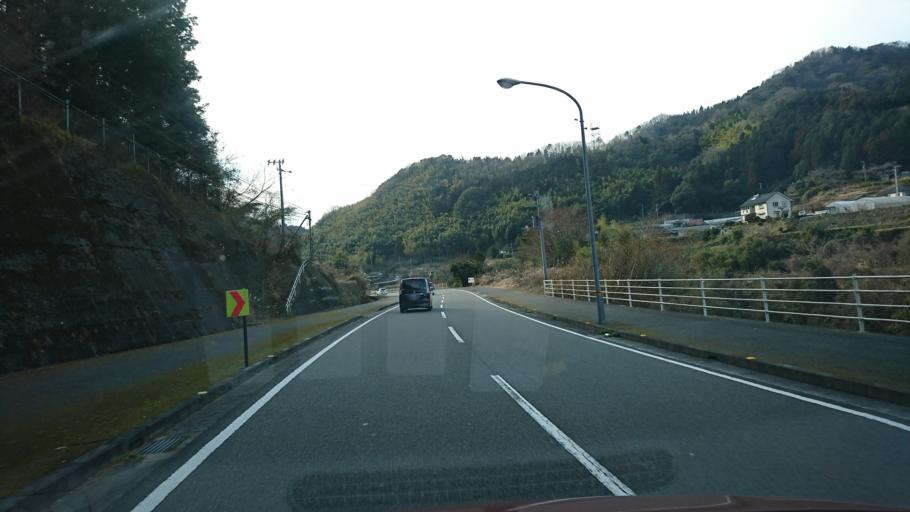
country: JP
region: Ehime
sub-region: Shikoku-chuo Shi
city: Matsuyama
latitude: 33.8988
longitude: 132.8645
